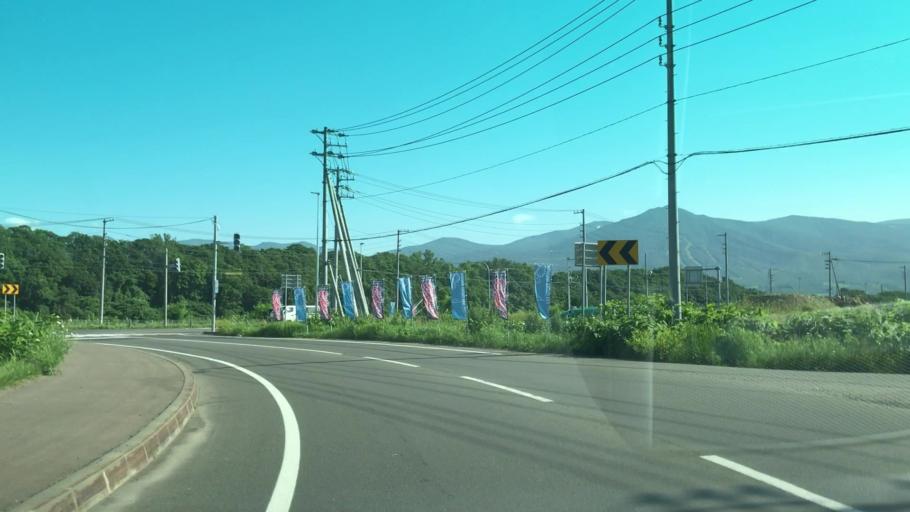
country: JP
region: Hokkaido
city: Iwanai
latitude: 42.9987
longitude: 140.5387
